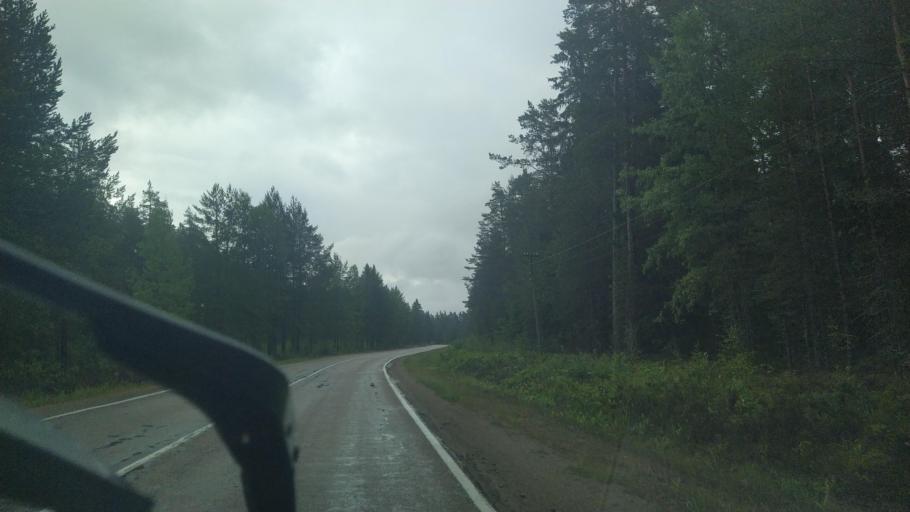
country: RU
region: Leningrad
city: Priozersk
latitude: 60.9788
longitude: 30.2731
